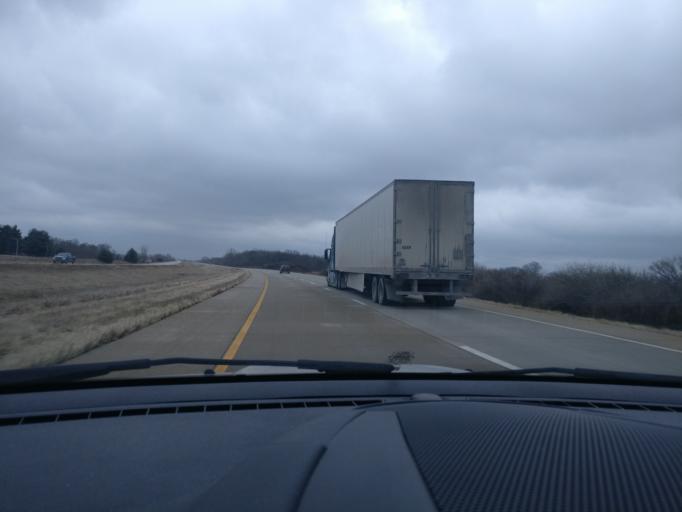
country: US
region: Illinois
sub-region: Whiteside County
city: Prophetstown
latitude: 41.7293
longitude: -89.9081
